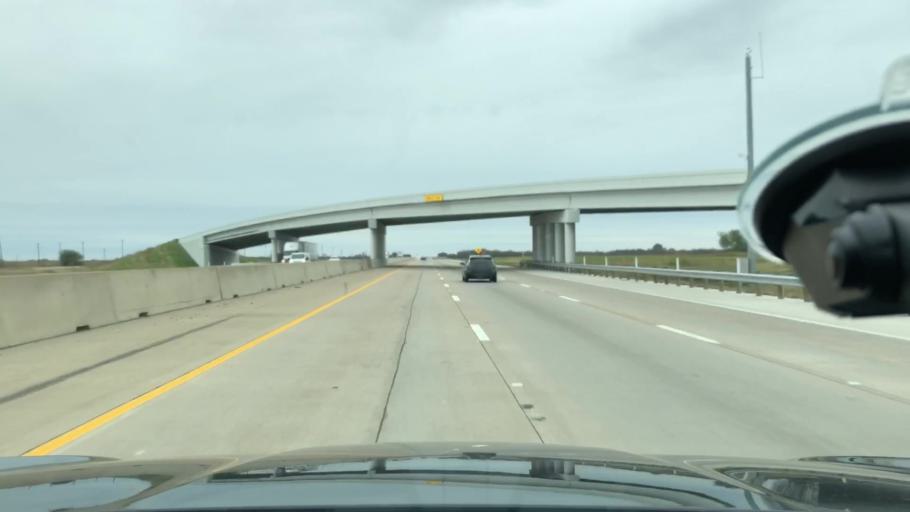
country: US
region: Texas
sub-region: Ellis County
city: Nash
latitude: 32.2585
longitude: -96.8732
